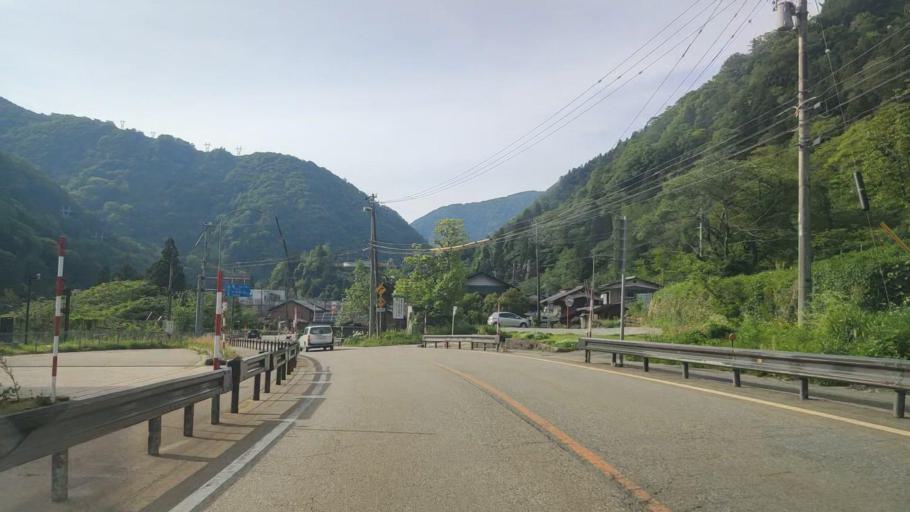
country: JP
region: Toyama
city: Yatsuomachi-higashikumisaka
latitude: 36.4327
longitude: 137.2781
